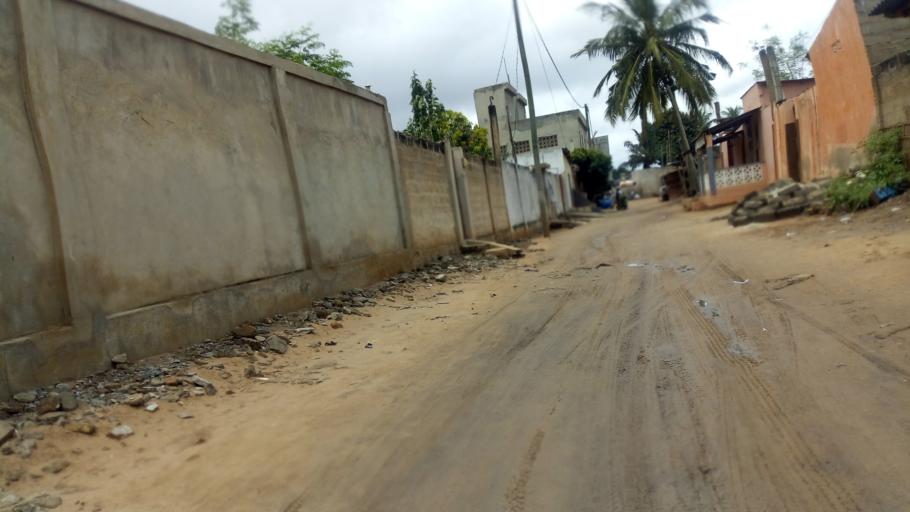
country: TG
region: Maritime
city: Lome
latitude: 6.1834
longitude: 1.1651
